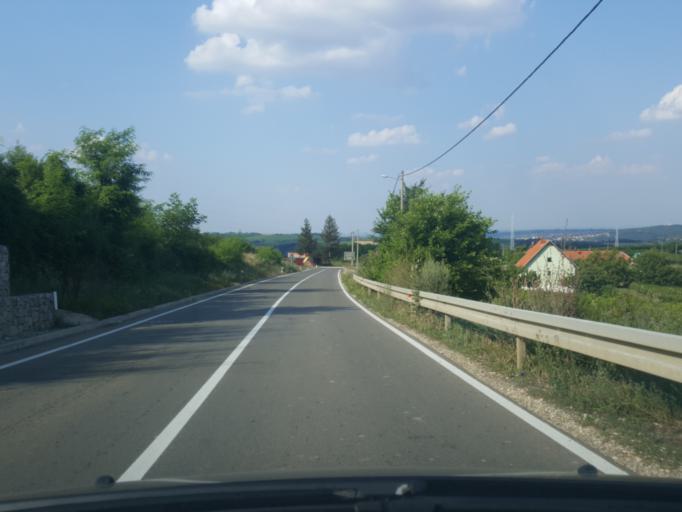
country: RS
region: Central Serbia
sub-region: Sumadijski Okrug
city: Topola
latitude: 44.2261
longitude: 20.6312
